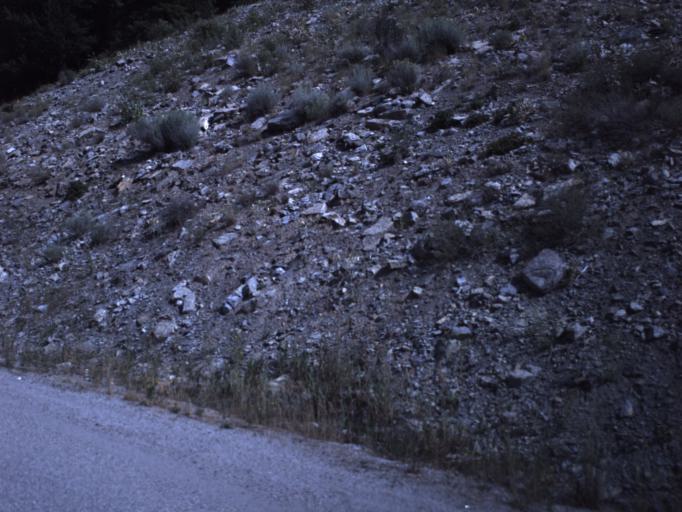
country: US
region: Utah
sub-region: Cache County
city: North Logan
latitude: 41.8237
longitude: -111.6043
